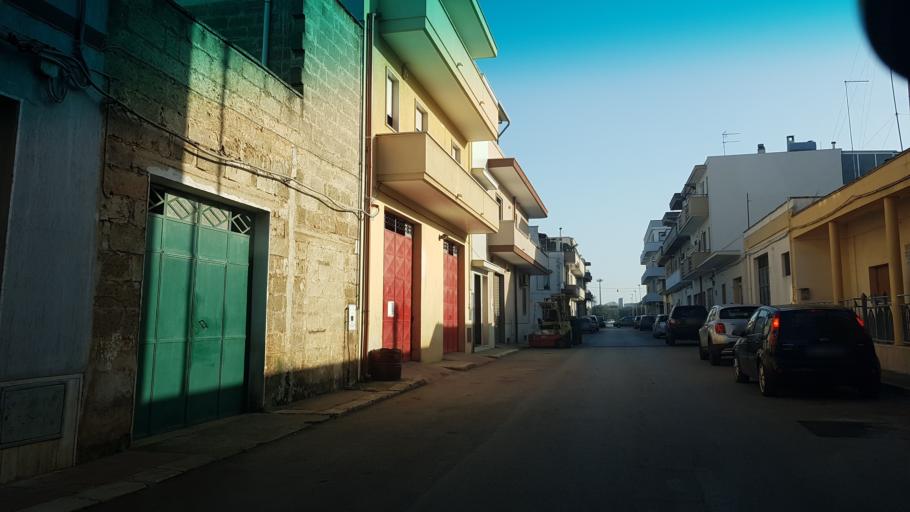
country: IT
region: Apulia
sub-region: Provincia di Brindisi
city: Carovigno
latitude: 40.7013
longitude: 17.6613
